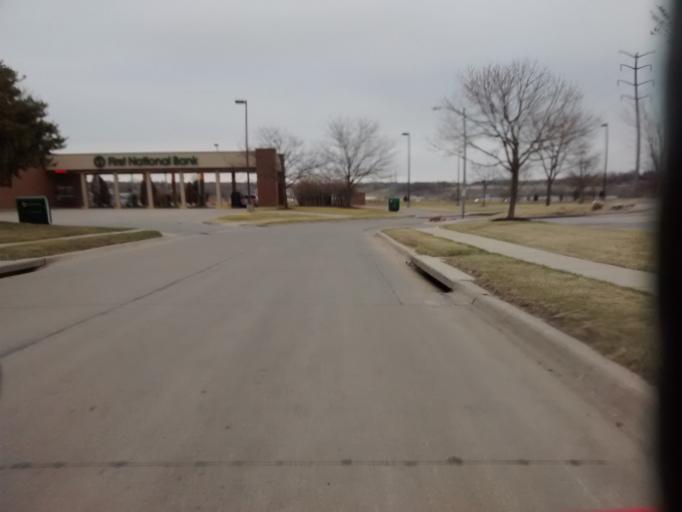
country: US
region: Nebraska
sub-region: Sarpy County
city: Offutt Air Force Base
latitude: 41.1581
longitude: -95.9417
